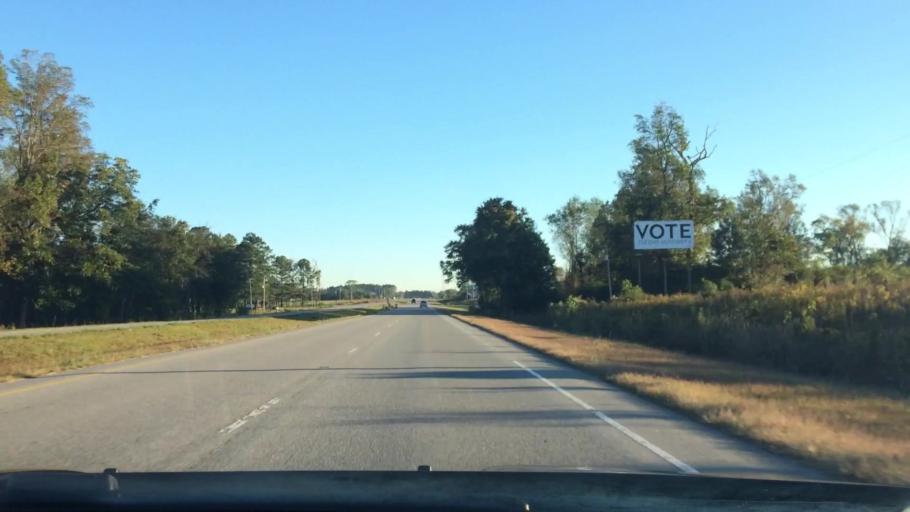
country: US
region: North Carolina
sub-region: Pitt County
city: Winterville
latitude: 35.5069
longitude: -77.4190
